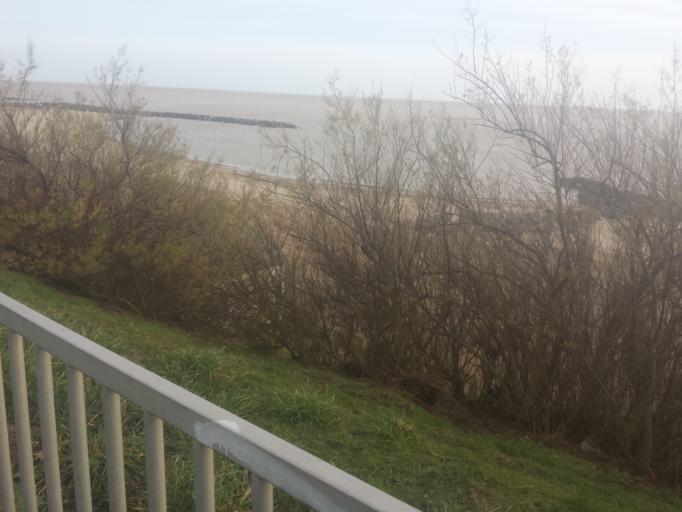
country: GB
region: England
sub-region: Essex
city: Frinton-on-Sea
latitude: 51.8080
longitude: 1.2131
